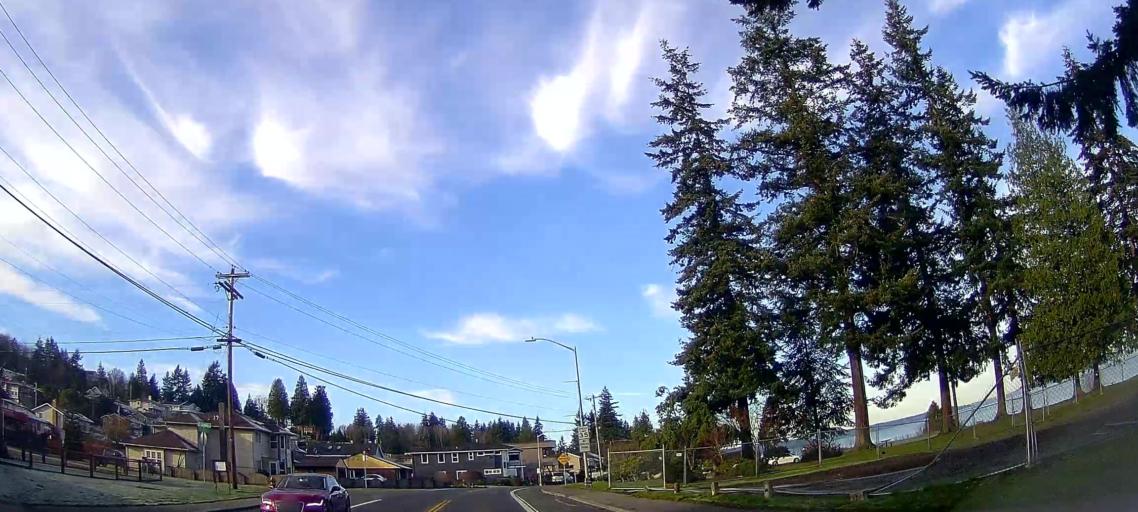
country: US
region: Washington
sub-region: Snohomish County
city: Everett
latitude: 47.9568
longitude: -122.2506
